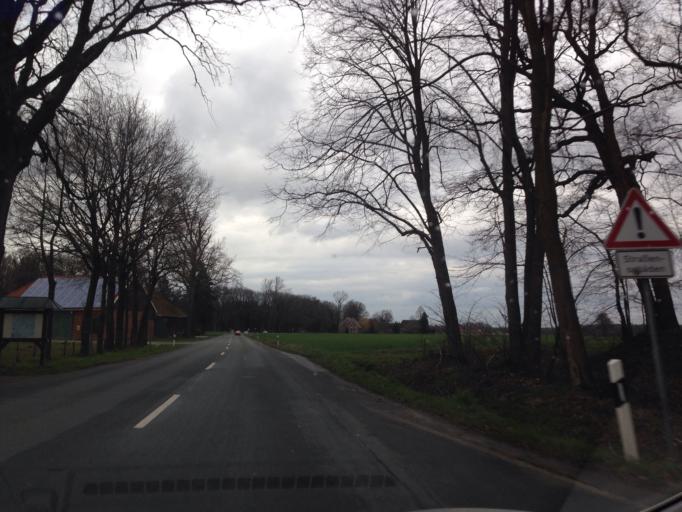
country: DE
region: North Rhine-Westphalia
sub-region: Regierungsbezirk Munster
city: Senden
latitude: 51.8543
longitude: 7.5470
